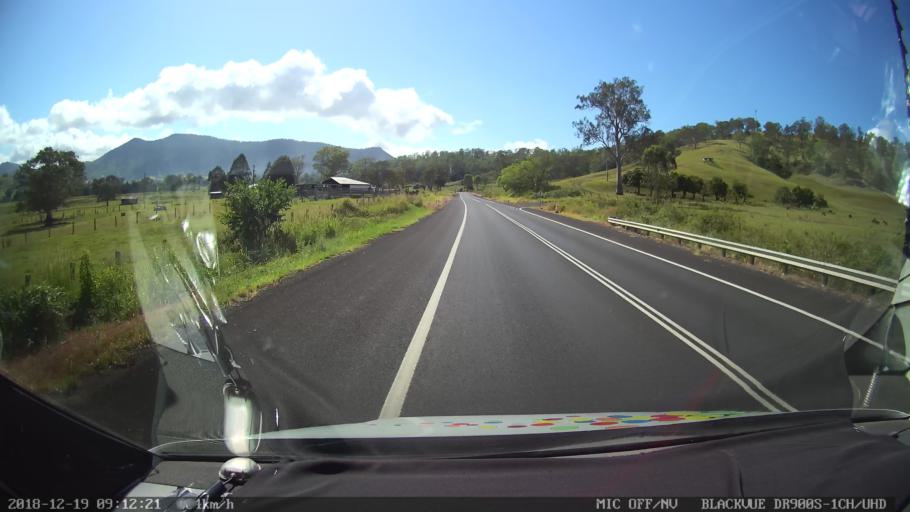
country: AU
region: New South Wales
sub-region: Kyogle
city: Kyogle
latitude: -28.4968
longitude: 152.9486
